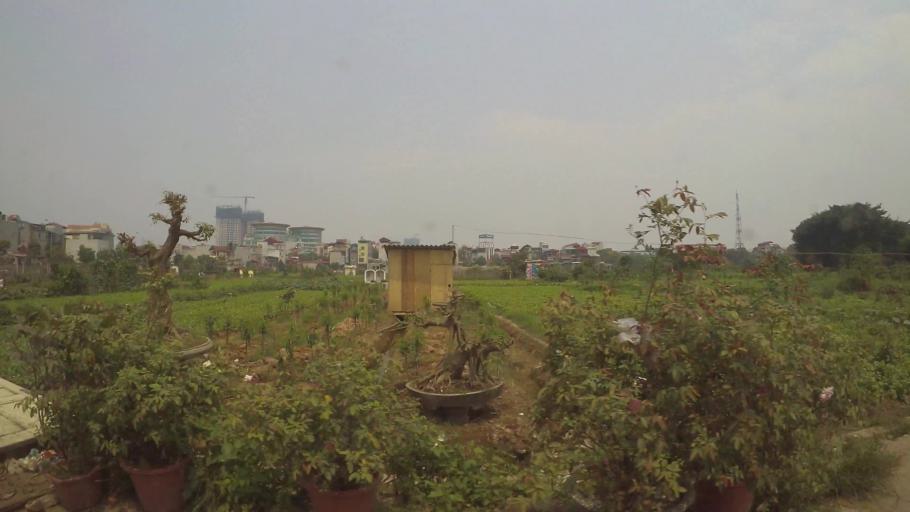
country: VN
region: Ha Noi
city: Van Dien
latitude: 20.9477
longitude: 105.8419
